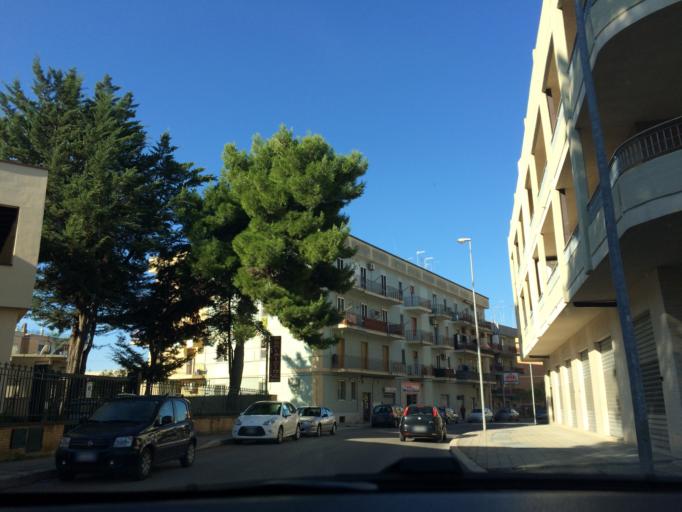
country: IT
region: Basilicate
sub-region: Provincia di Matera
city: Matera
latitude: 40.6767
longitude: 16.5972
